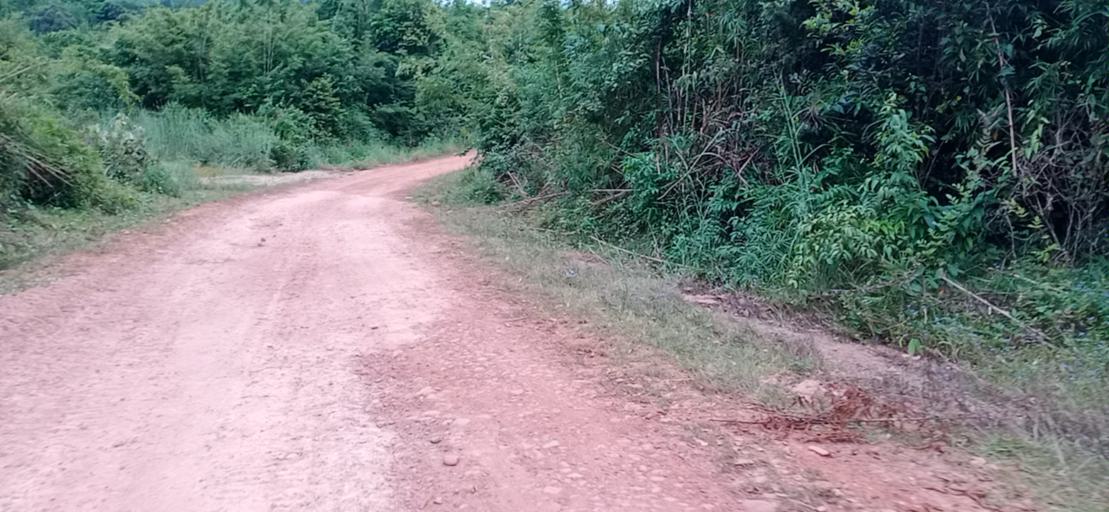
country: TH
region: Changwat Bueng Kan
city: Pak Khat
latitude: 18.5545
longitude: 103.1727
